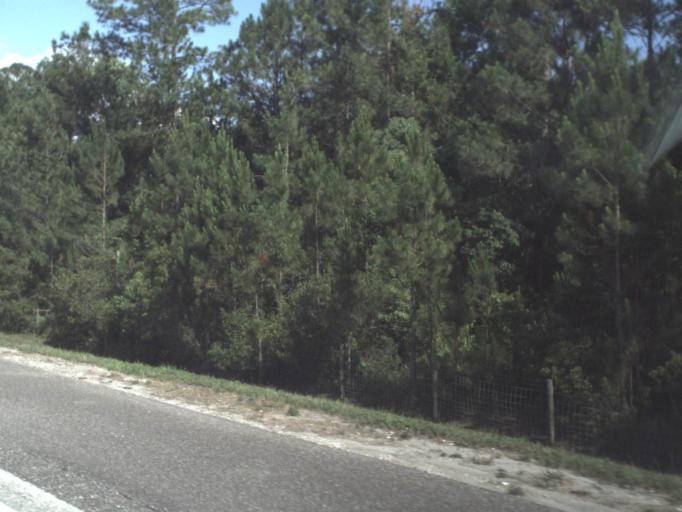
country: US
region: Florida
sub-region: Duval County
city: Jacksonville
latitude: 30.2499
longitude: -81.5701
